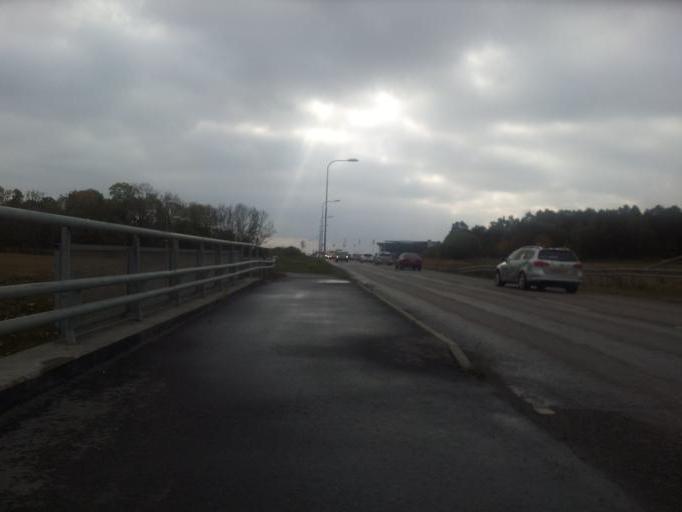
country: SE
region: Uppsala
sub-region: Uppsala Kommun
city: Uppsala
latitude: 59.8826
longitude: 17.6723
